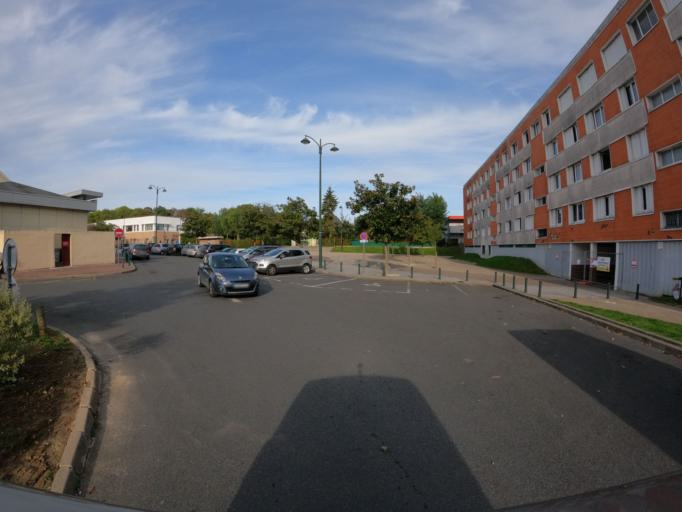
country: FR
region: Ile-de-France
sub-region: Departement de Seine-et-Marne
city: Pontault-Combault
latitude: 48.7994
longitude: 2.6085
